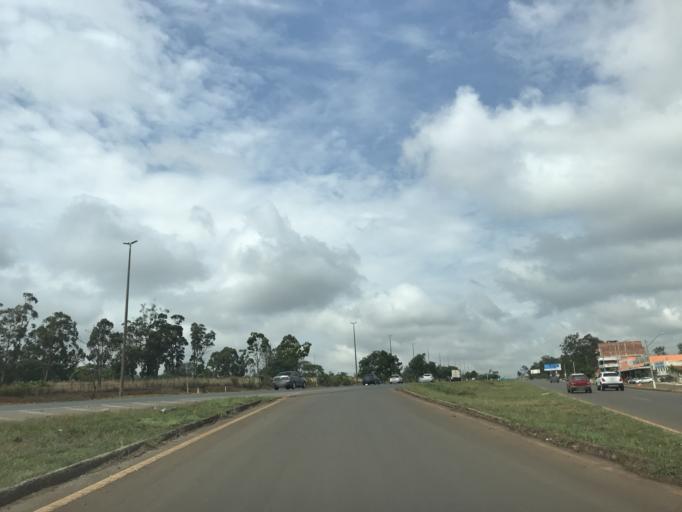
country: BR
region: Federal District
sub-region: Brasilia
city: Brasilia
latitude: -15.6824
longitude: -47.8406
